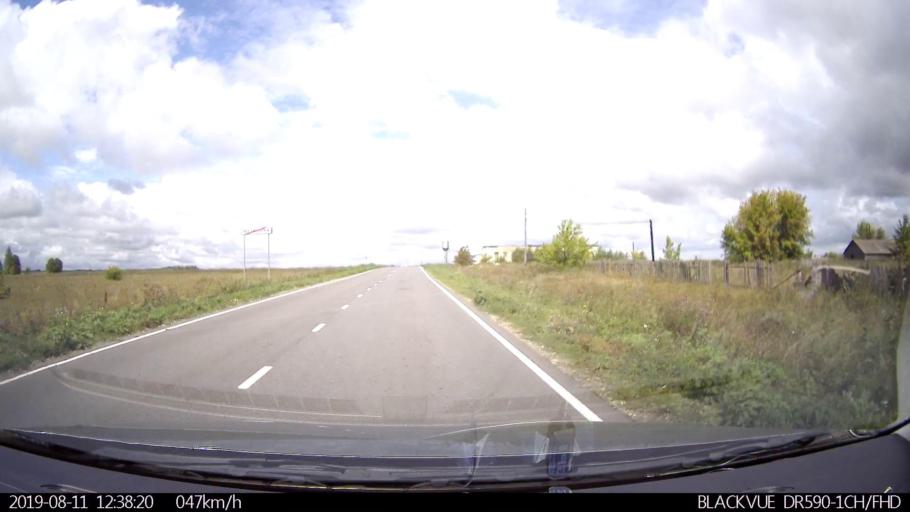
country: RU
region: Ulyanovsk
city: Ignatovka
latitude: 53.8264
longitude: 47.8076
